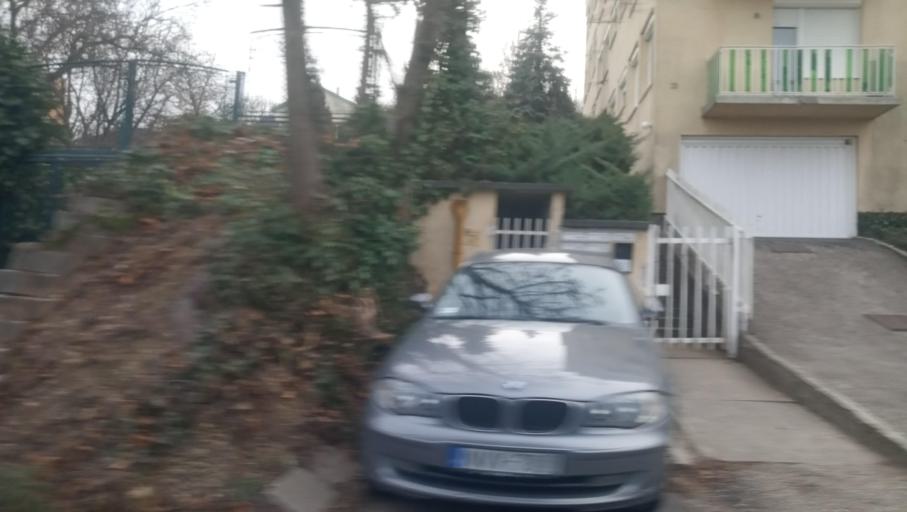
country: HU
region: Budapest
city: Budapest II. keruelet
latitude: 47.5294
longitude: 19.0230
